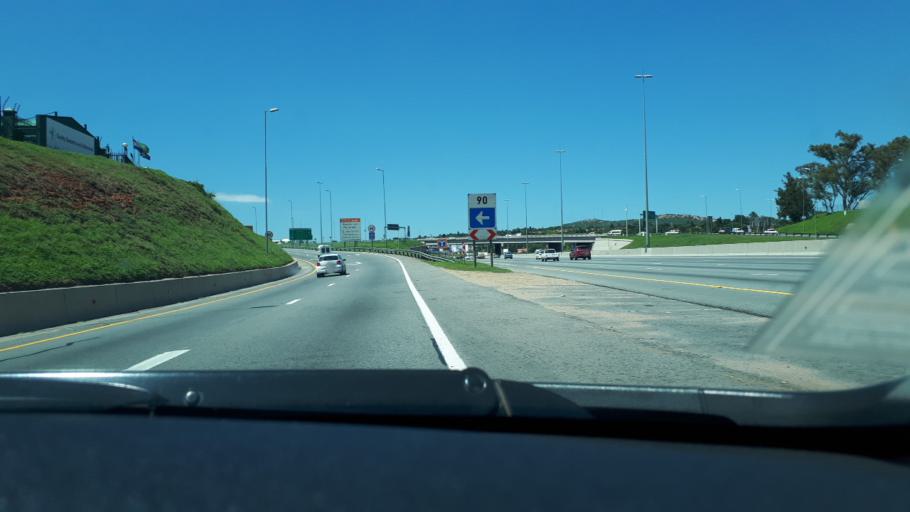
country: ZA
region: Gauteng
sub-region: City of Johannesburg Metropolitan Municipality
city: Roodepoort
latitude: -26.0702
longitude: 27.9755
